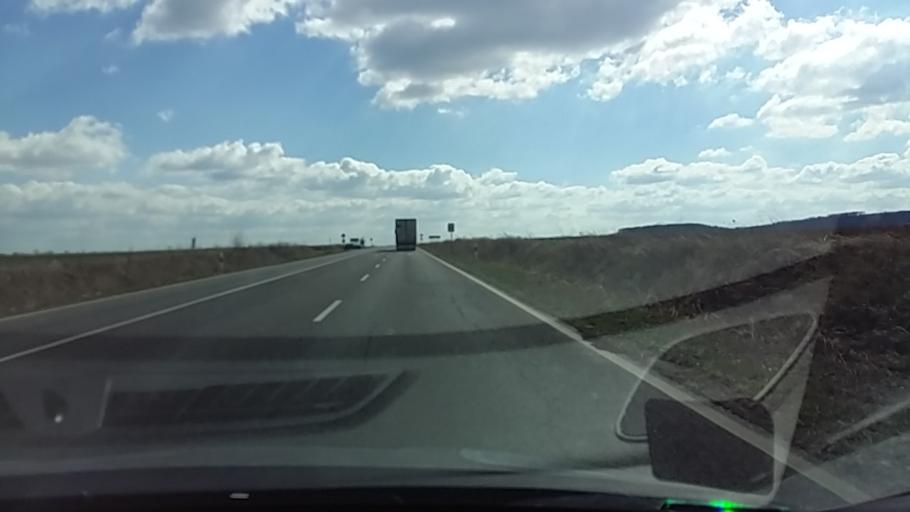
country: HU
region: Baranya
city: Kozarmisleny
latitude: 46.0373
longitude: 18.2726
